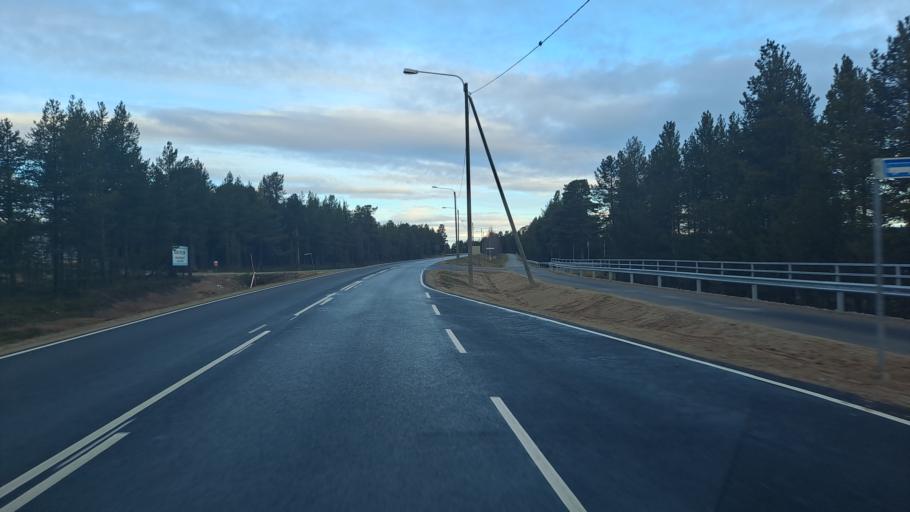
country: FI
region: Lapland
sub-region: Pohjois-Lappi
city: Inari
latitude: 68.8983
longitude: 27.0829
